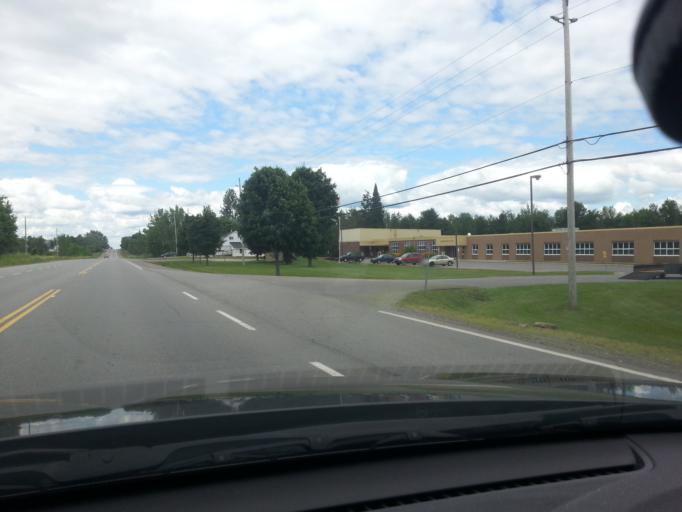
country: CA
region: Ontario
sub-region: Lanark County
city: Smiths Falls
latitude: 44.8360
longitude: -76.0728
